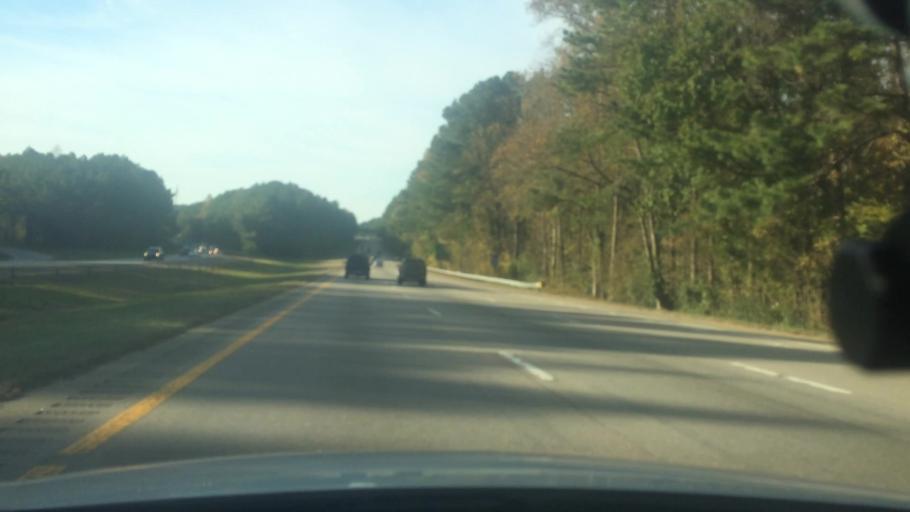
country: US
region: North Carolina
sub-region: Wake County
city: Cary
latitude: 35.8124
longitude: -78.7454
